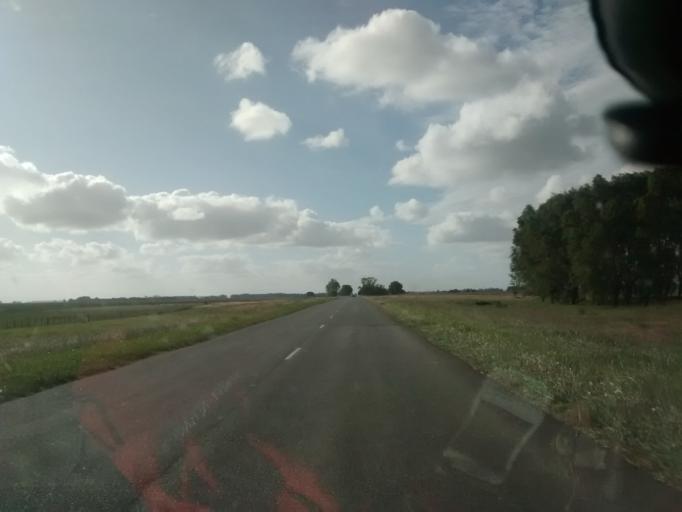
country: AR
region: Buenos Aires
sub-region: Partido de Ayacucho
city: Ayacucho
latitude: -37.2577
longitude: -58.4835
